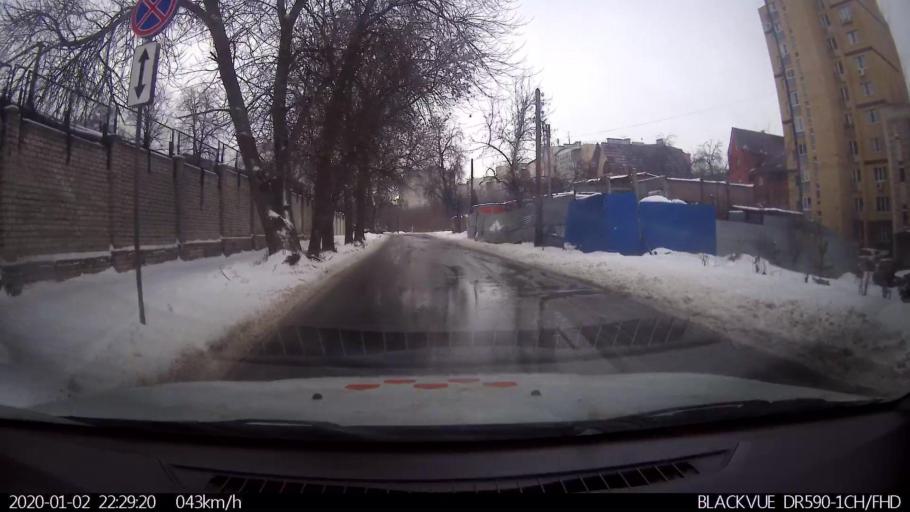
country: RU
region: Nizjnij Novgorod
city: Nizhniy Novgorod
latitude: 56.3175
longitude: 44.0430
